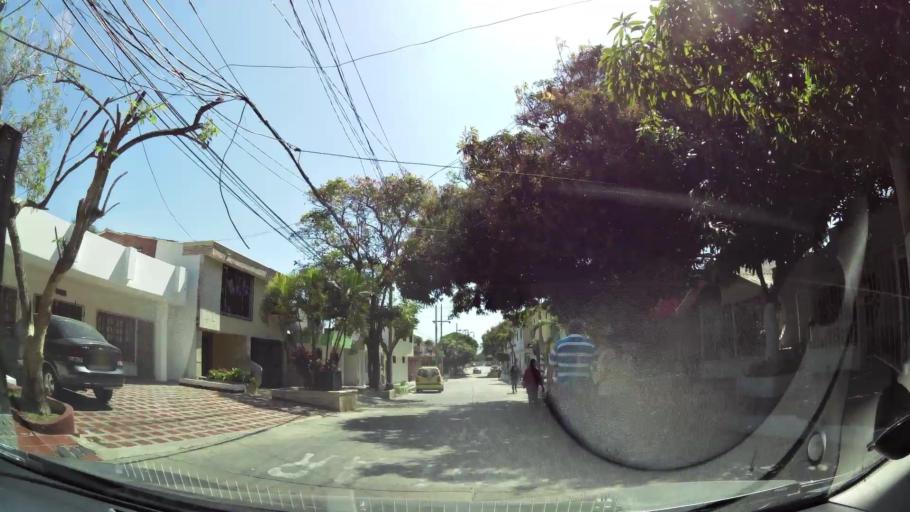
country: CO
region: Atlantico
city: Barranquilla
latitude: 11.0066
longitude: -74.7957
